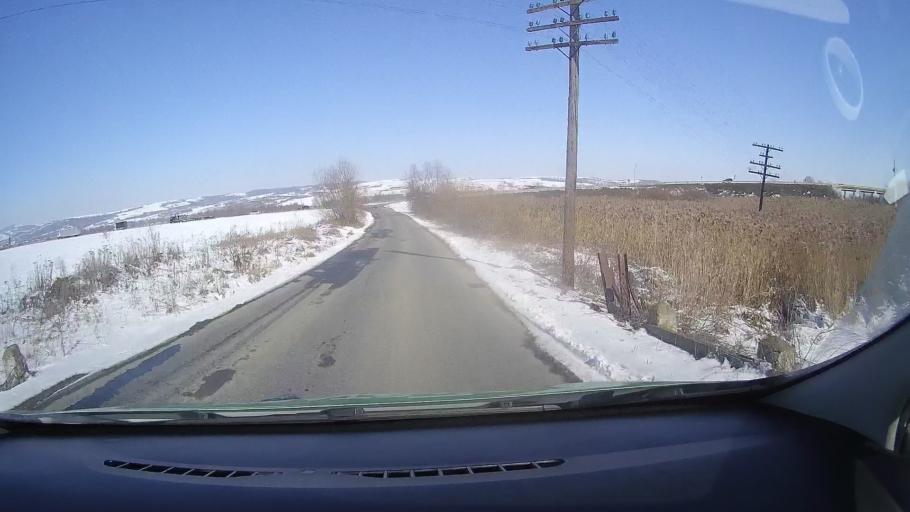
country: RO
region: Brasov
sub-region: Comuna Mandra
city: Mandra
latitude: 45.8311
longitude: 25.0137
